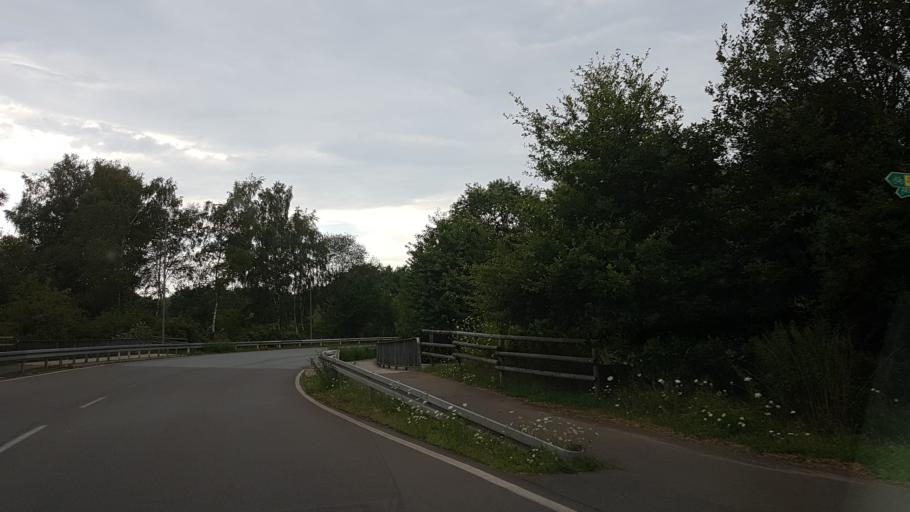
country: DE
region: Saarland
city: Homburg
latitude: 49.3061
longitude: 7.3274
